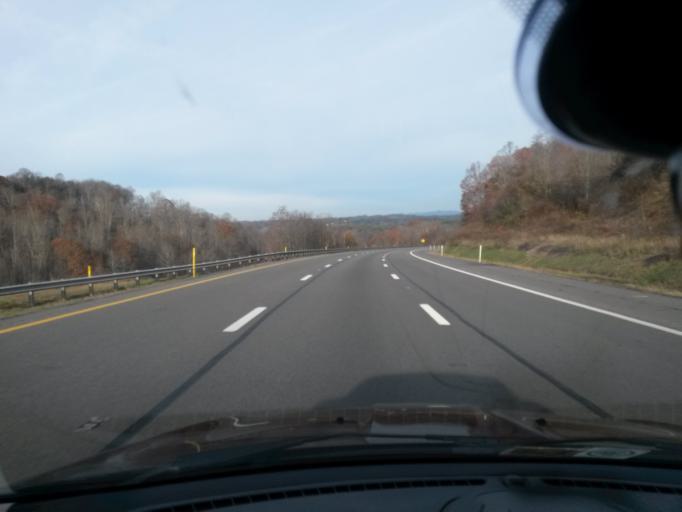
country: US
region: West Virginia
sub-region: Raleigh County
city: MacArthur
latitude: 37.7327
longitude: -81.2025
